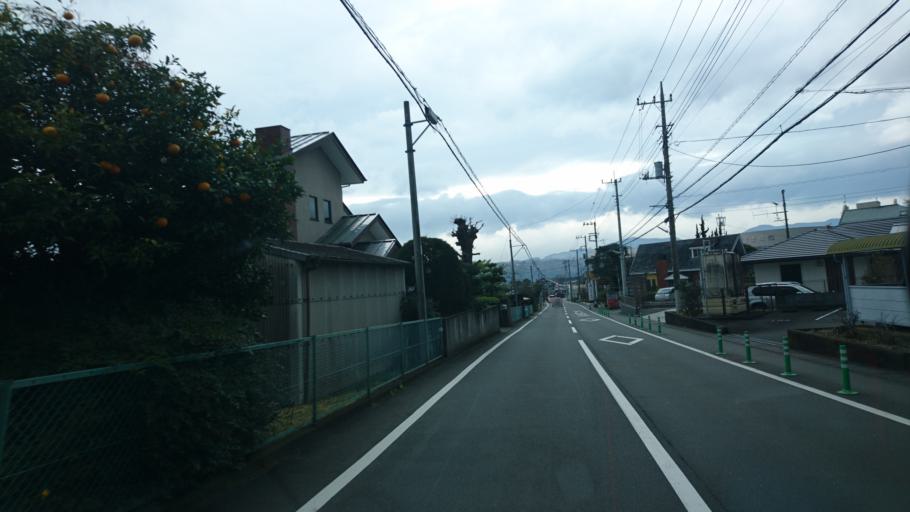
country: JP
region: Shizuoka
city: Fujinomiya
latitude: 35.2501
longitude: 138.6127
